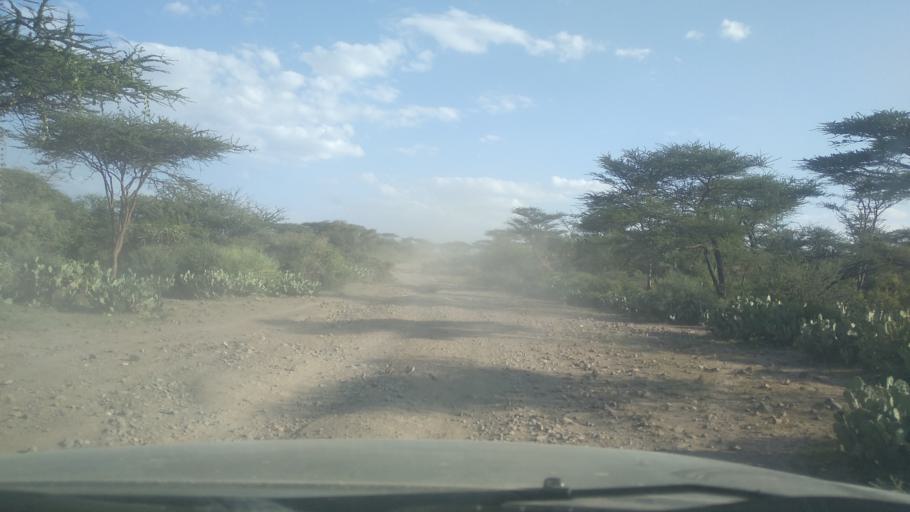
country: ET
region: Oromiya
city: Hirna
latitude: 9.4215
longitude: 40.9620
